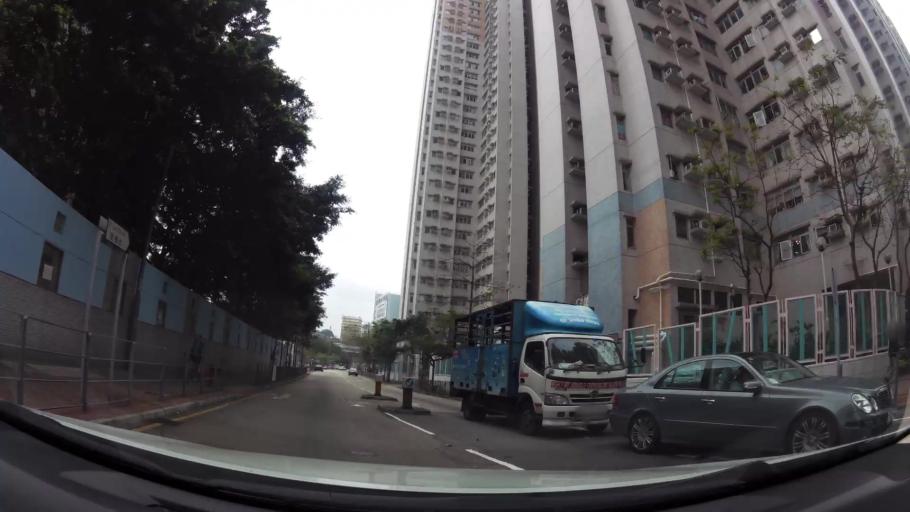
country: HK
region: Wanchai
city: Wan Chai
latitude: 22.2822
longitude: 114.2284
